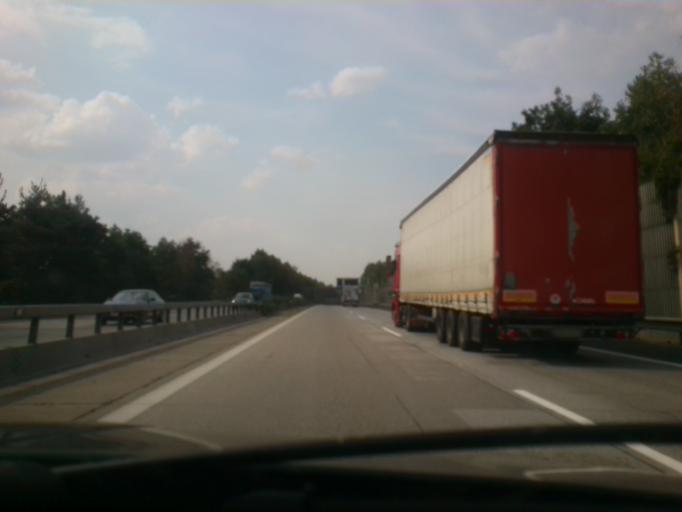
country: CZ
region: Central Bohemia
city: Ondrejov
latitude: 49.8911
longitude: 14.7510
